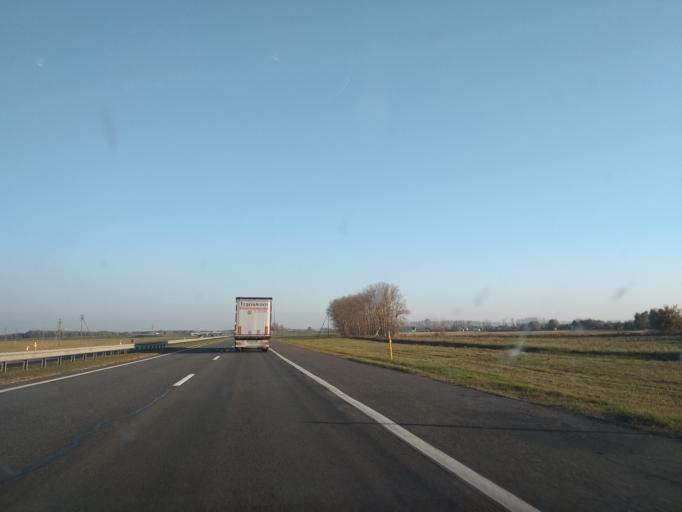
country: BY
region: Brest
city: Kobryn
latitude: 52.1887
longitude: 24.3143
